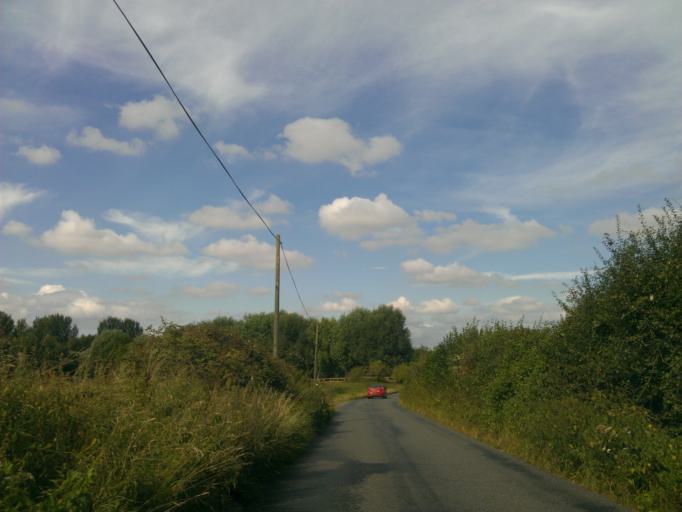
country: GB
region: England
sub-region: Essex
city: Sible Hedingham
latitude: 51.9816
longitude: 0.6031
